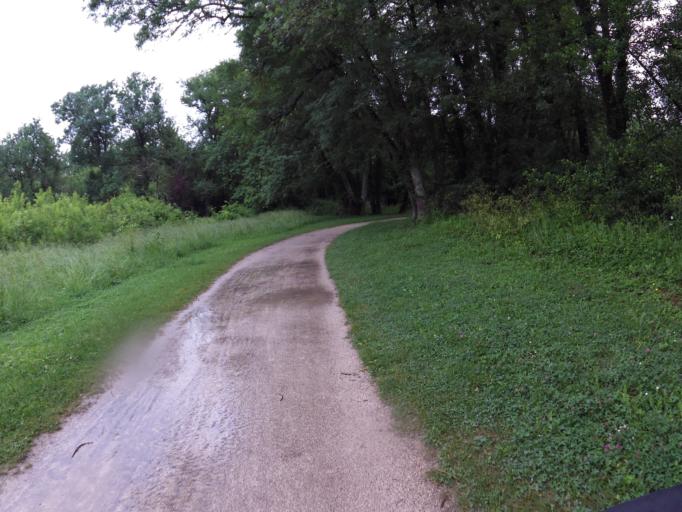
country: FR
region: Poitou-Charentes
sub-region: Departement de la Charente
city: Angouleme
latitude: 45.6625
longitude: 0.1586
